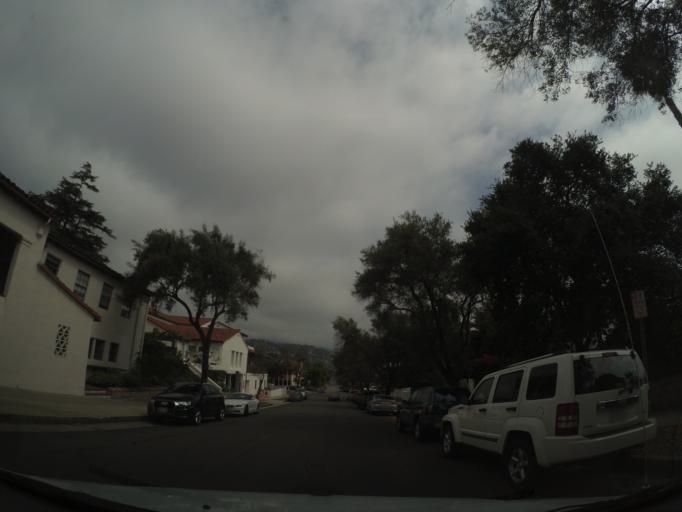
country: US
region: California
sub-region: Santa Barbara County
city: Santa Barbara
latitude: 34.4222
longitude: -119.6966
